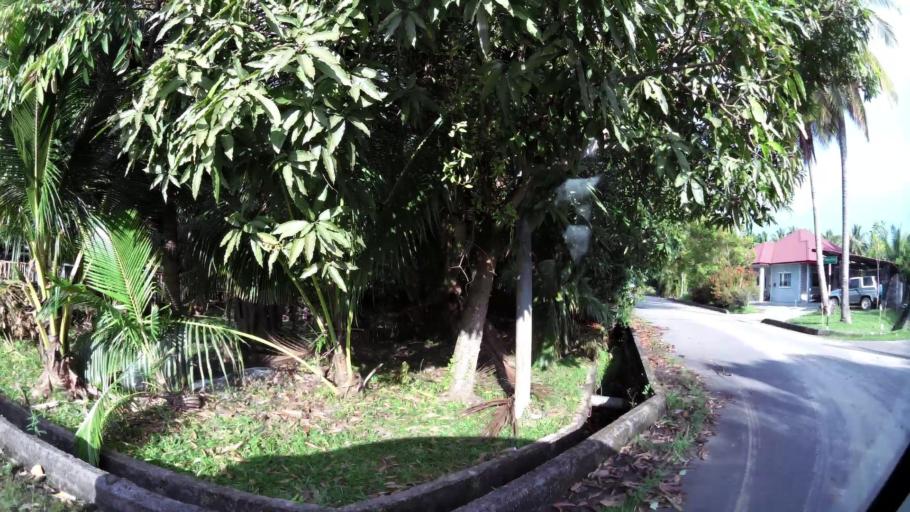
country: BN
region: Brunei and Muara
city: Bandar Seri Begawan
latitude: 4.9518
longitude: 115.0244
